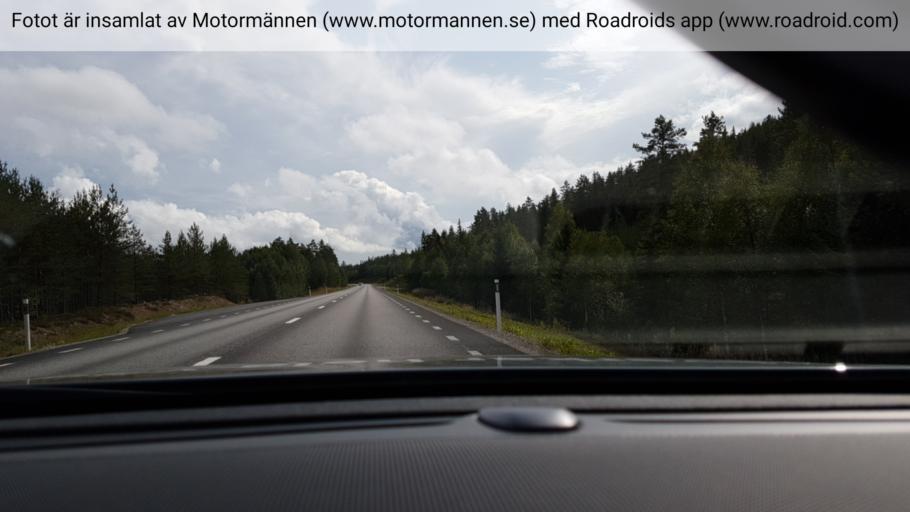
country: SE
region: Dalarna
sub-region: Rattviks Kommun
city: Raettvik
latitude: 60.8084
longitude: 15.2619
